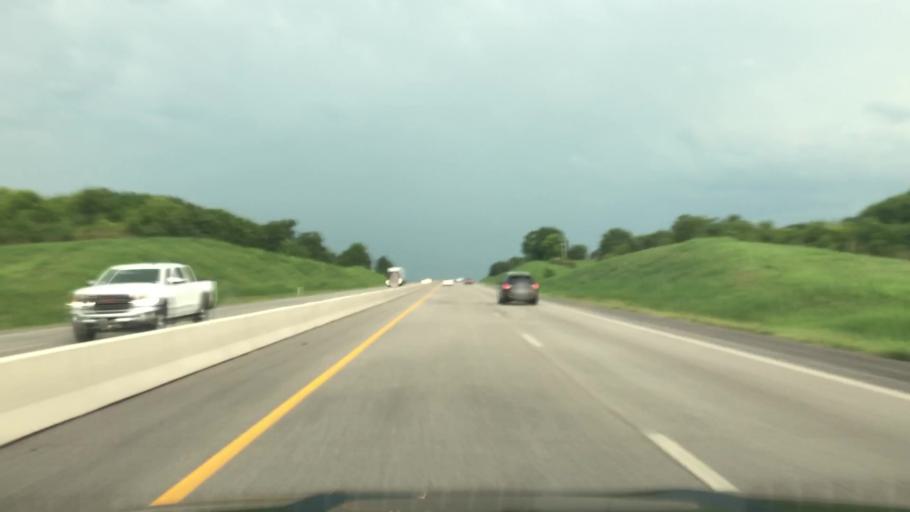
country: US
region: Oklahoma
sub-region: Rogers County
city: Justice
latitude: 36.3240
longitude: -95.5396
